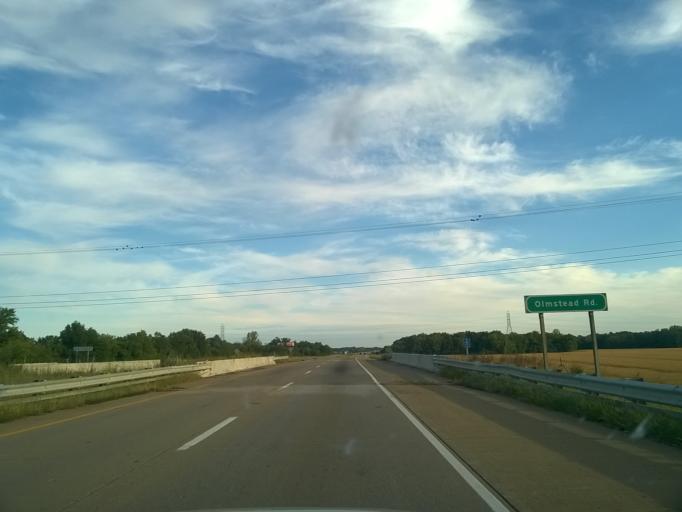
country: US
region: Indiana
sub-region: Vanderburgh County
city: Melody Hill
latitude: 38.0283
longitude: -87.4720
